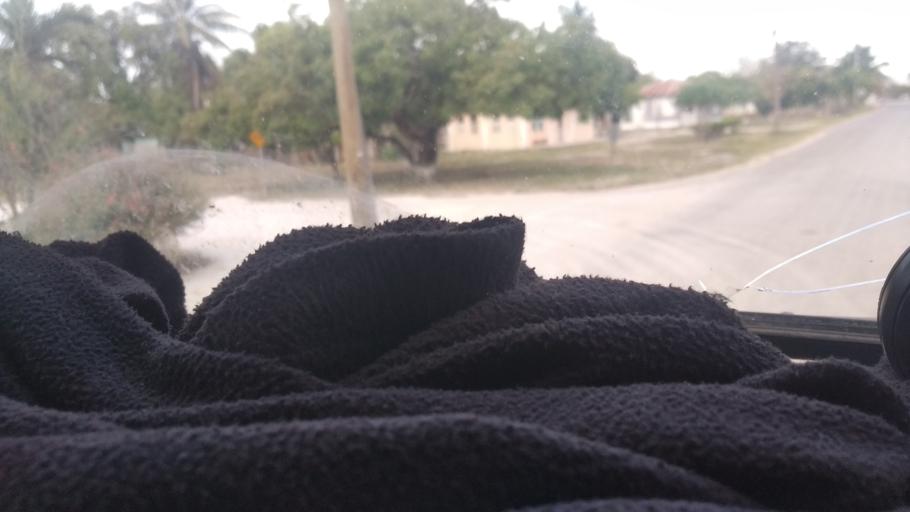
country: BZ
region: Corozal
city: Corozal
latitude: 18.3049
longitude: -88.5195
